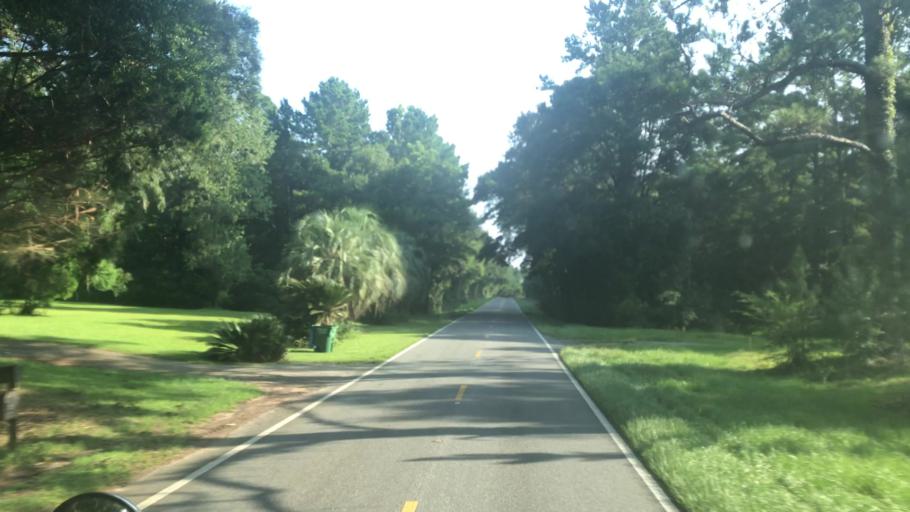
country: US
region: Florida
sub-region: Gadsden County
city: Quincy
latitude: 30.6916
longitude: -84.5384
